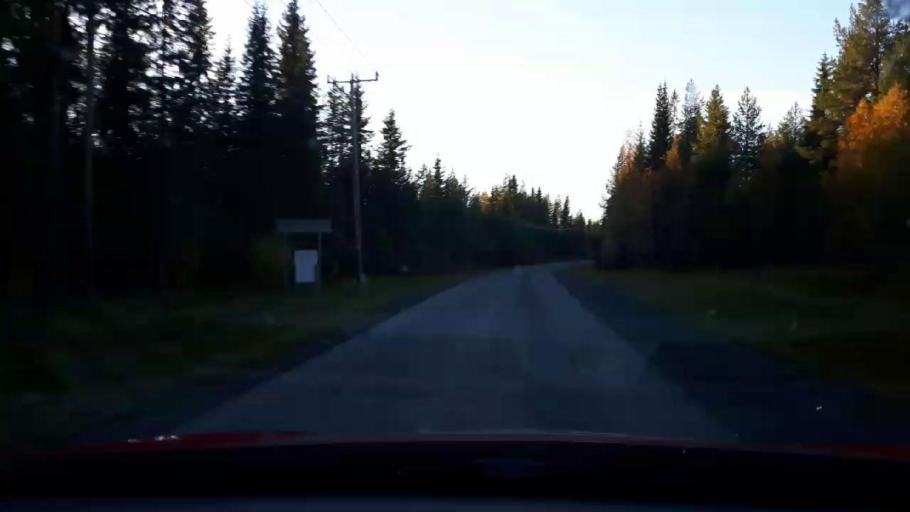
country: SE
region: Jaemtland
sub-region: Krokoms Kommun
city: Krokom
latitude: 63.4330
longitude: 14.4288
